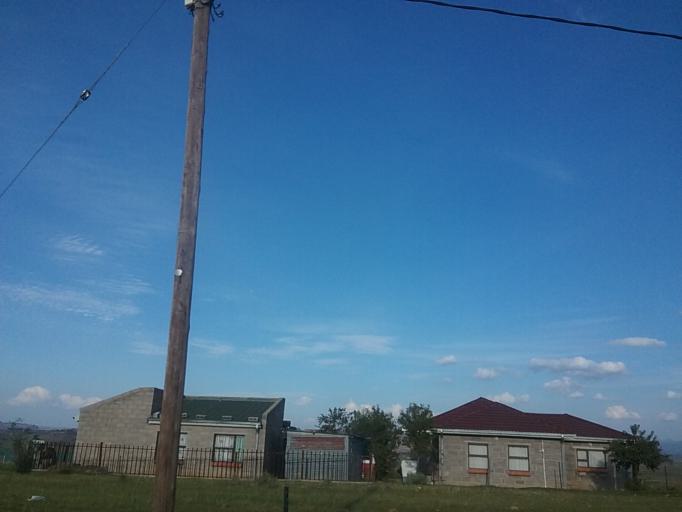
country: LS
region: Berea
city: Teyateyaneng
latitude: -29.1298
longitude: 27.7600
